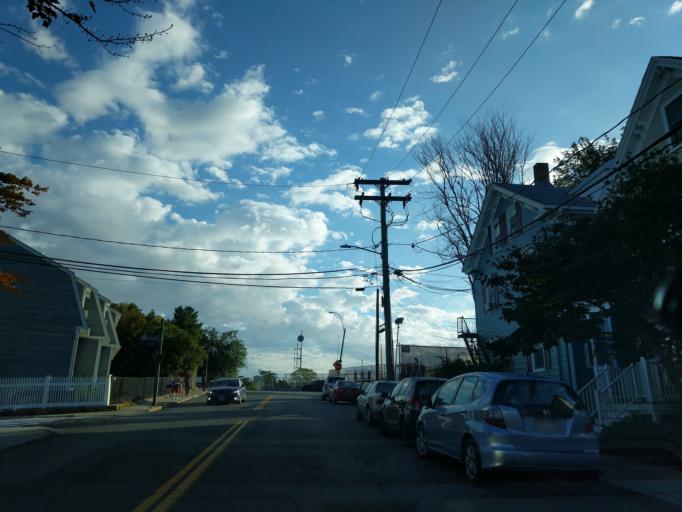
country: US
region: Massachusetts
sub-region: Middlesex County
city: Cambridge
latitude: 42.3775
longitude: -71.0966
